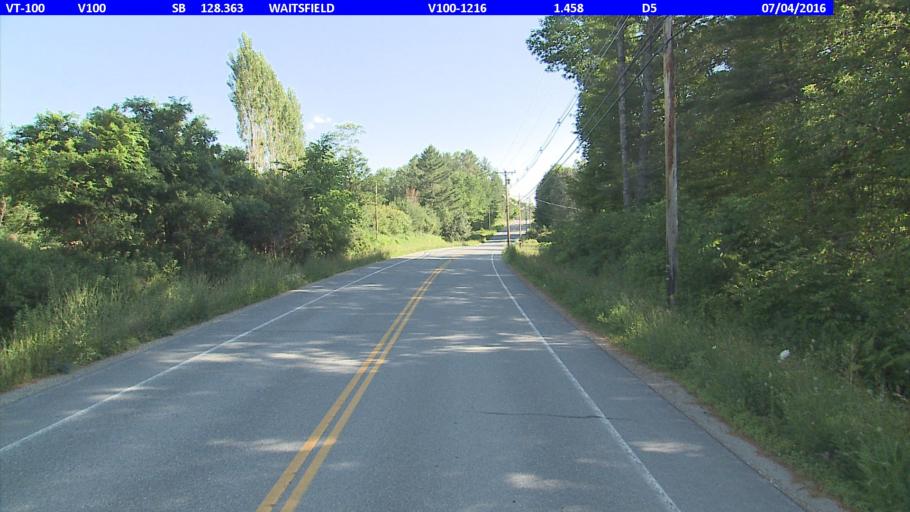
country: US
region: Vermont
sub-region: Washington County
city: Northfield
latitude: 44.1664
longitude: -72.8317
